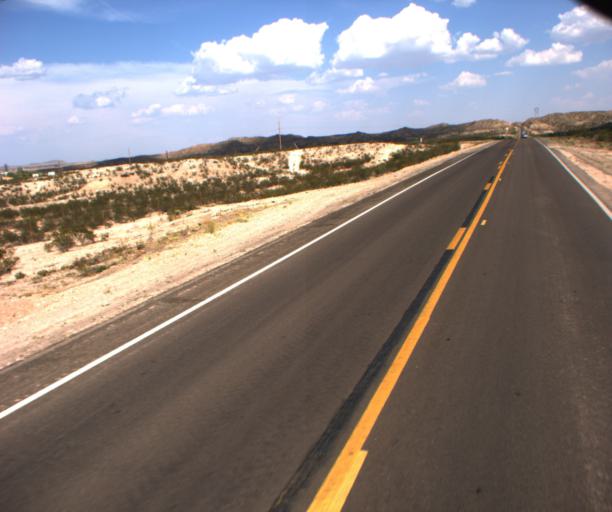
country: US
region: Arizona
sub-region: Greenlee County
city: Clifton
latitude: 32.7638
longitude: -109.1438
